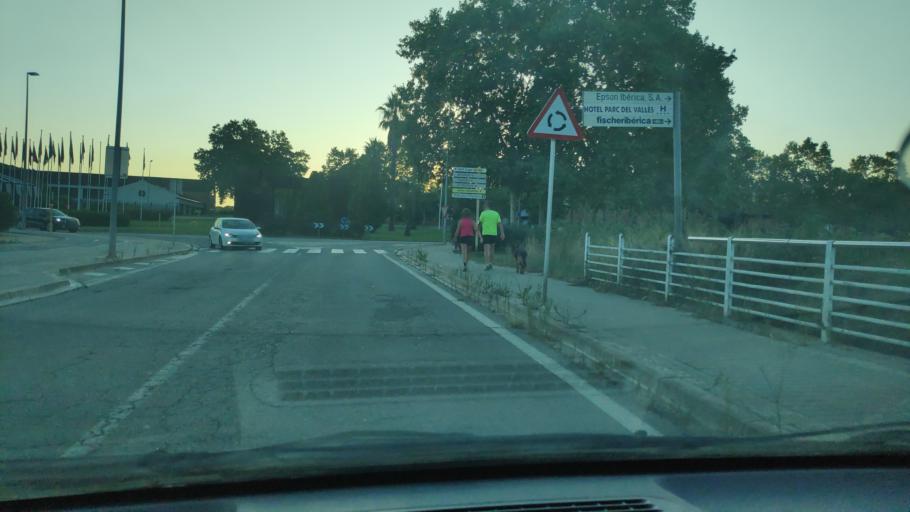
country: ES
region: Catalonia
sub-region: Provincia de Barcelona
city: Cerdanyola del Valles
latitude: 41.4855
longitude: 2.1291
